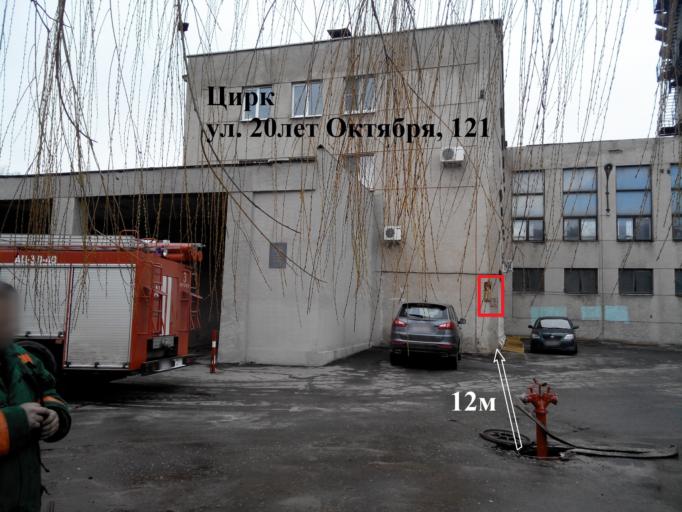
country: RU
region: Voronezj
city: Voronezh
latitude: 51.6553
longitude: 39.1851
